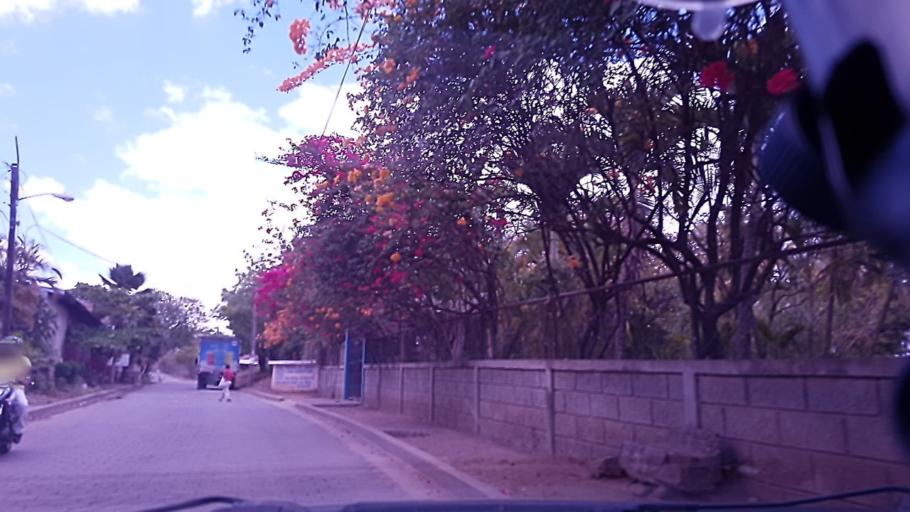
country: NI
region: Esteli
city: Condega
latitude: 13.3670
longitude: -86.3982
